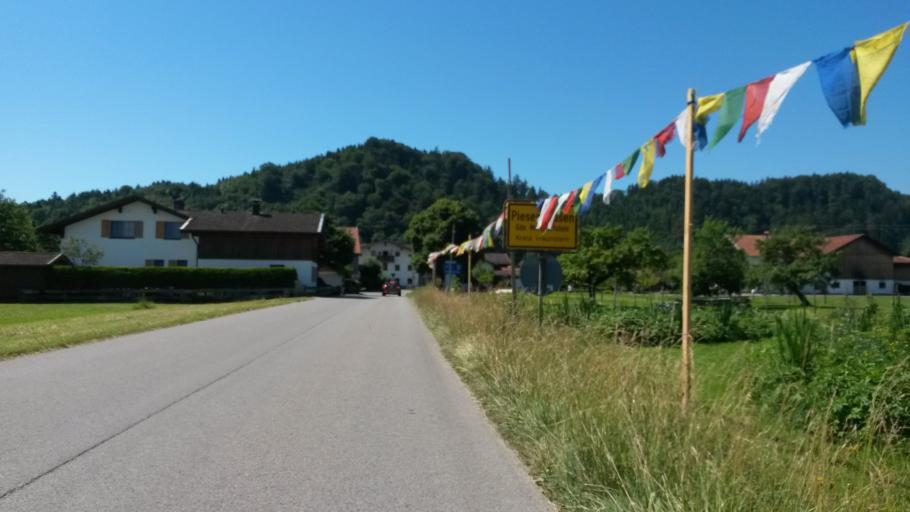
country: DE
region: Bavaria
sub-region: Upper Bavaria
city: Marquartstein
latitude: 47.7645
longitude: 12.4524
